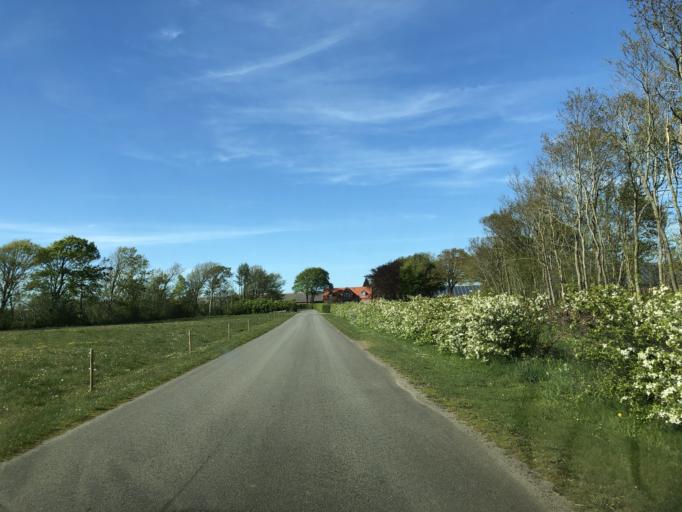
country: DK
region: Central Jutland
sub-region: Ringkobing-Skjern Kommune
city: Videbaek
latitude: 56.1896
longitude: 8.5156
